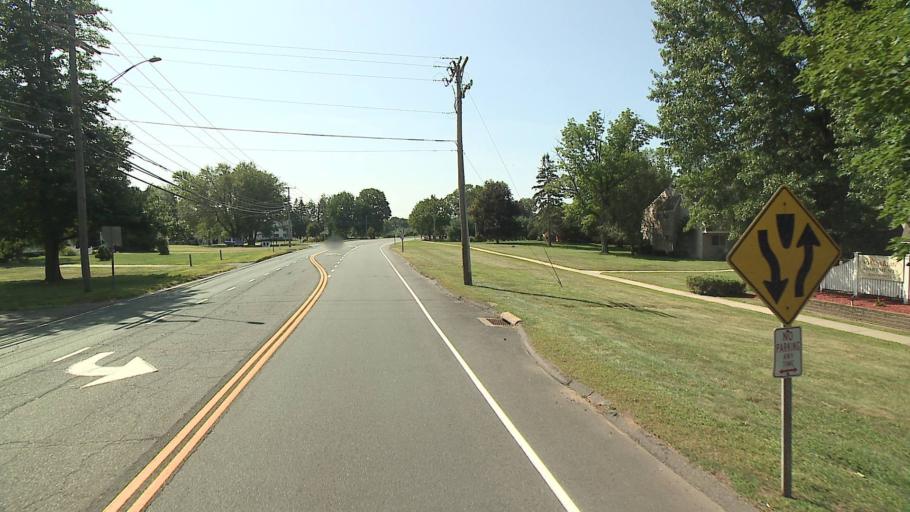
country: US
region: Connecticut
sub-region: Hartford County
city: Enfield
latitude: 41.9652
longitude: -72.5931
